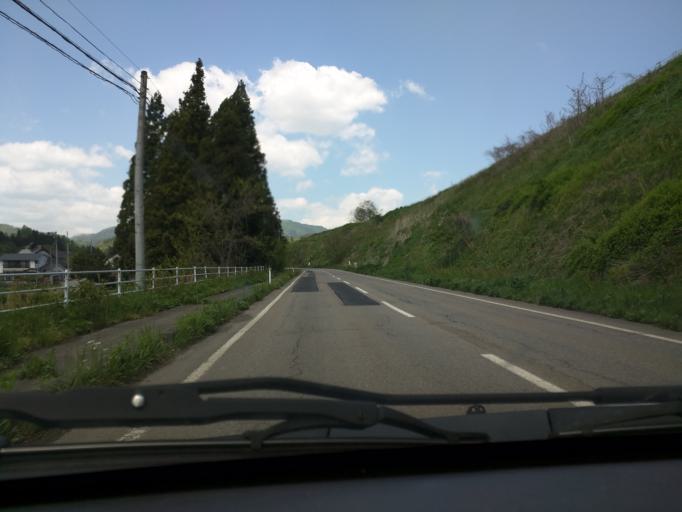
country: JP
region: Fukushima
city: Kitakata
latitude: 37.6422
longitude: 139.7790
